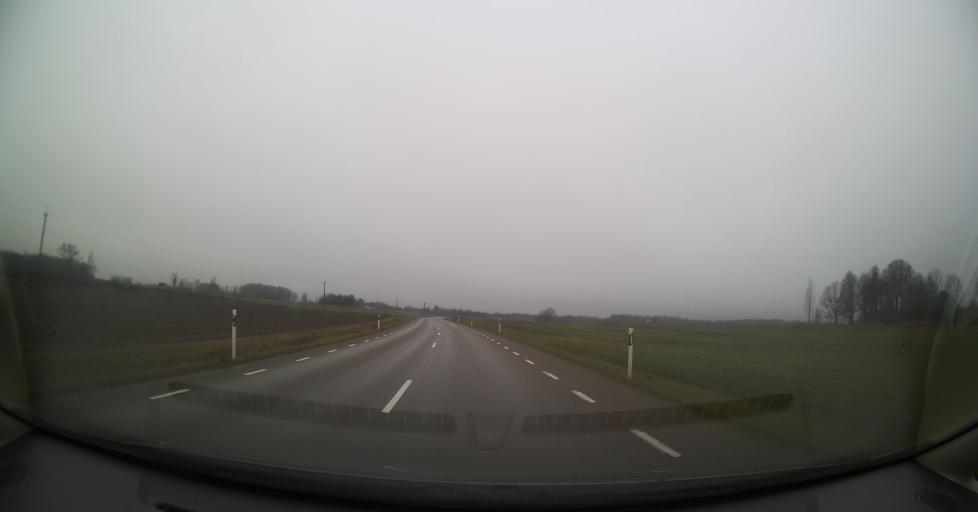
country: EE
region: Tartu
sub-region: Tartu linn
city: Tartu
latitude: 58.3965
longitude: 26.8406
